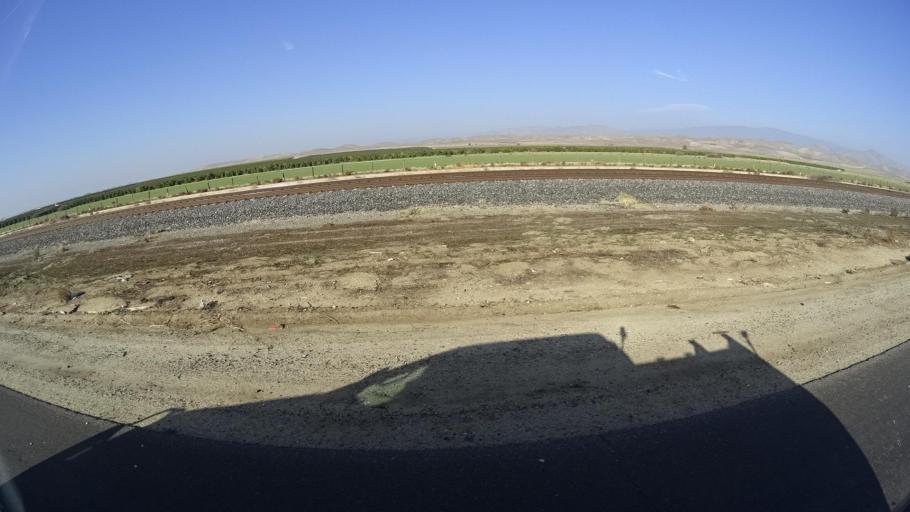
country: US
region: California
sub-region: Kern County
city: Lamont
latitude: 35.3378
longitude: -118.8289
